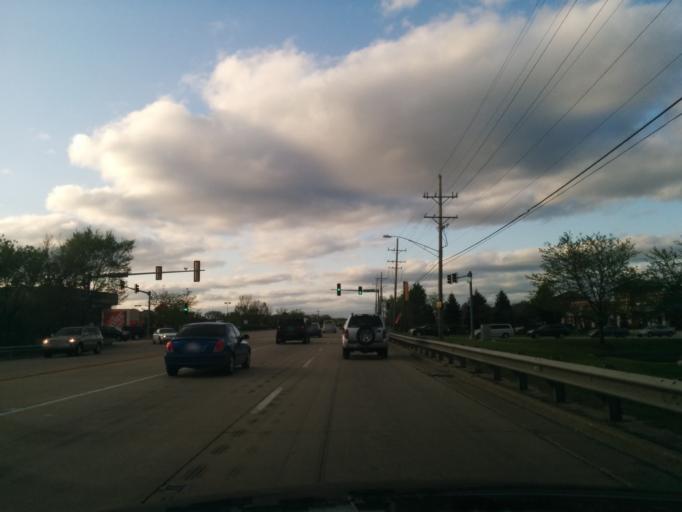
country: US
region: Illinois
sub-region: Cook County
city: Bartlett
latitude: 41.9712
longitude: -88.2068
